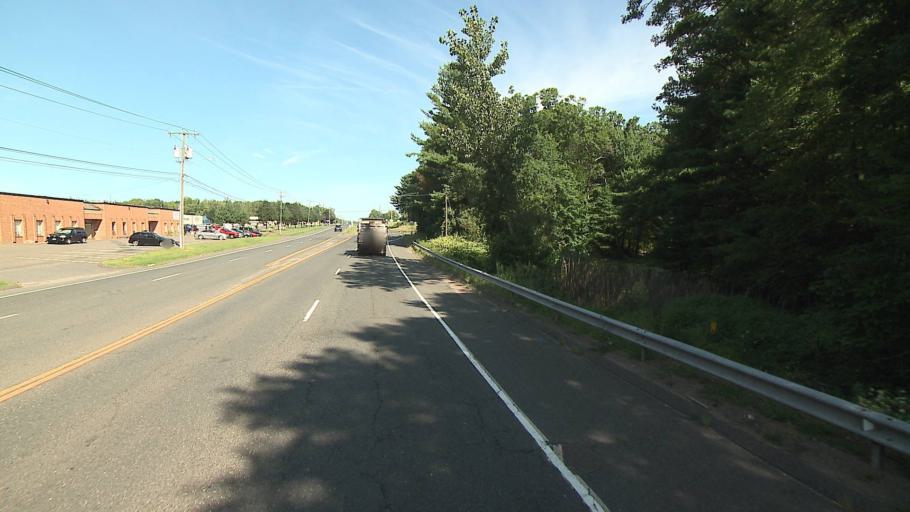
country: US
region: Connecticut
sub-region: Hartford County
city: Blue Hills
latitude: 41.8623
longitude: -72.7141
